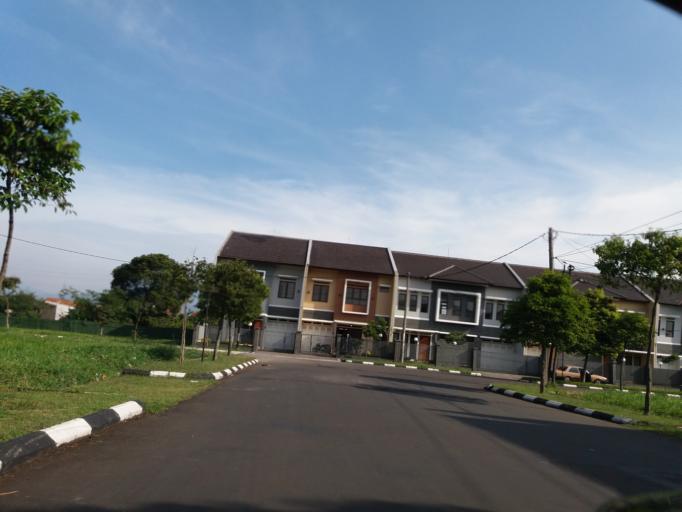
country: ID
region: West Java
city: Bandung
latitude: -6.9599
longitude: 107.6333
